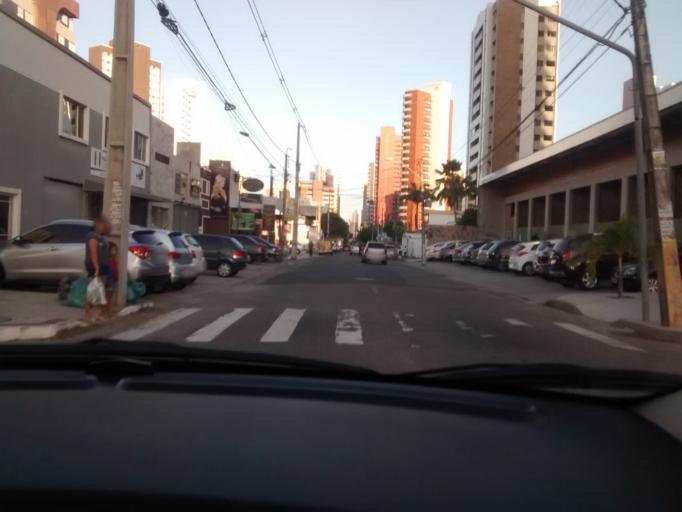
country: BR
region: Ceara
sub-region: Fortaleza
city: Fortaleza
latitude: -3.7389
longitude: -38.4970
